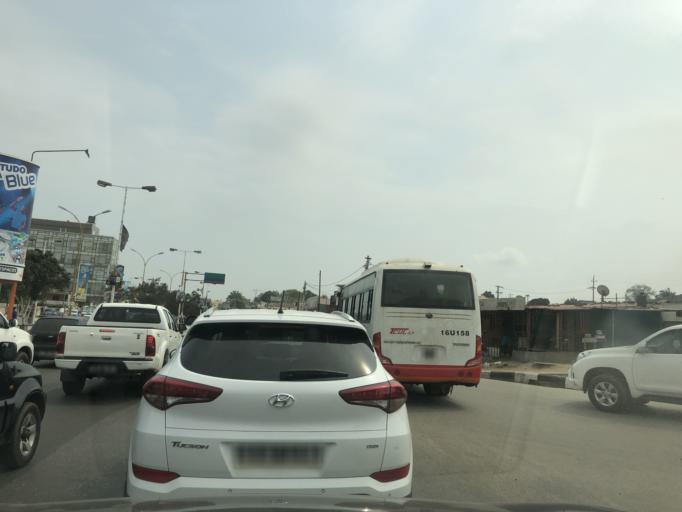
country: AO
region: Luanda
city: Luanda
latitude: -8.8469
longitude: 13.2120
